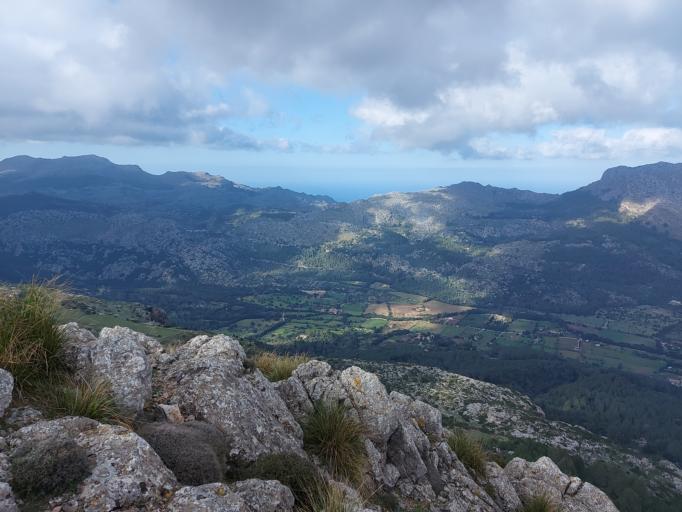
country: ES
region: Balearic Islands
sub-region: Illes Balears
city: Pollenca
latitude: 39.8516
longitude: 2.9681
